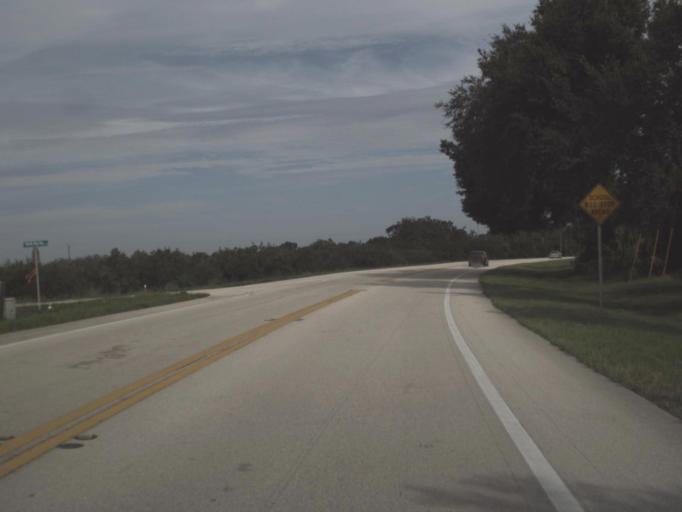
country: US
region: Florida
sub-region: DeSoto County
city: Southeast Arcadia
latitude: 27.1725
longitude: -81.8273
